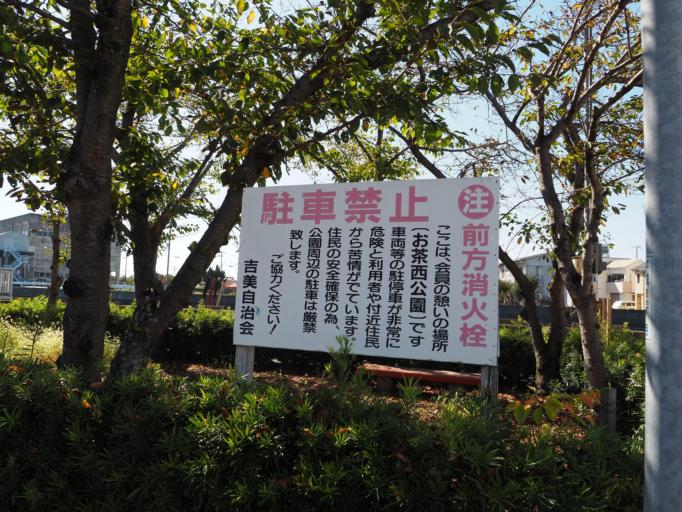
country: JP
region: Hyogo
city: Tatsunocho-tominaga
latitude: 34.7864
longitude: 134.6004
